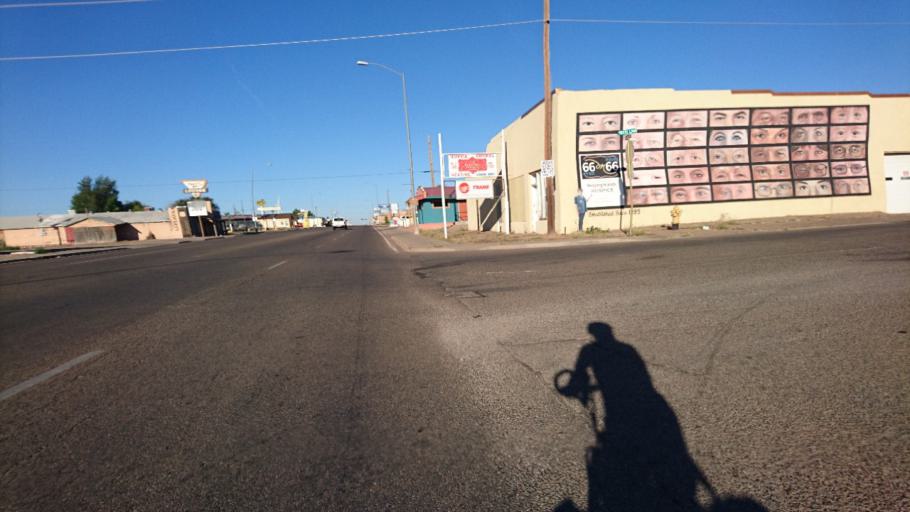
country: US
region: New Mexico
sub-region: Quay County
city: Tucumcari
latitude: 35.1719
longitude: -103.7197
